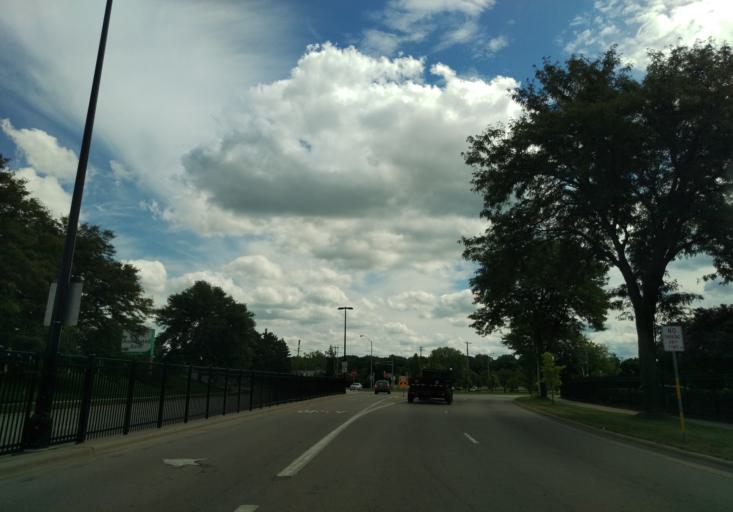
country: US
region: Wisconsin
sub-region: Dane County
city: Maple Bluff
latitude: 43.1285
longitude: -89.3574
